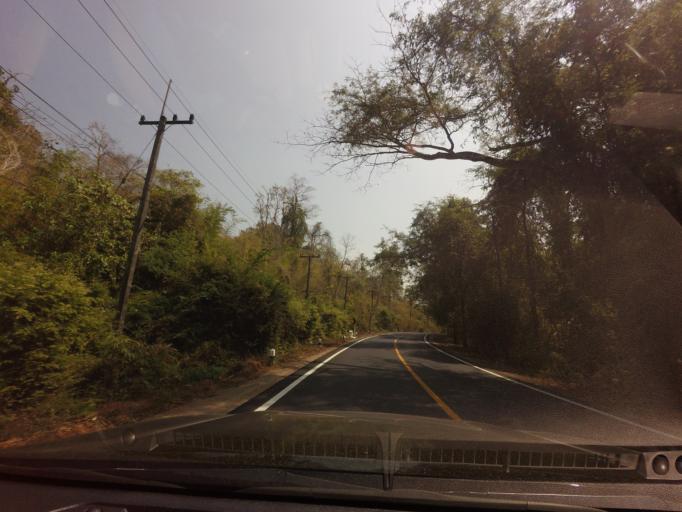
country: TH
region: Kanchanaburi
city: Thong Pha Phum
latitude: 14.7814
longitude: 98.5819
